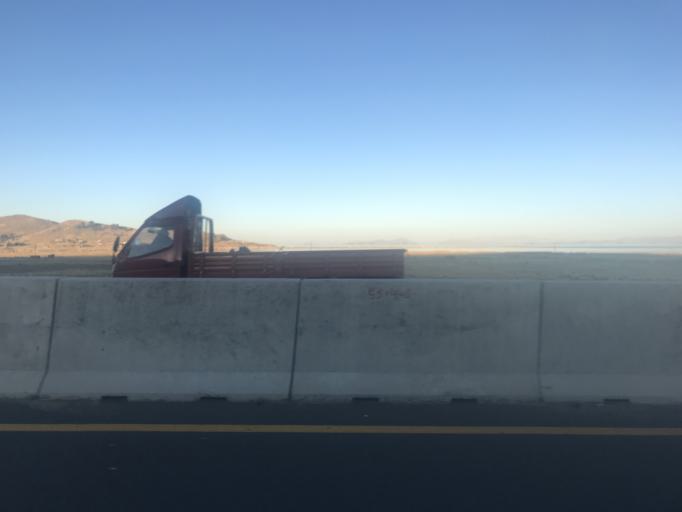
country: BO
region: La Paz
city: Huarina
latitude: -16.2199
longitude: -68.5865
